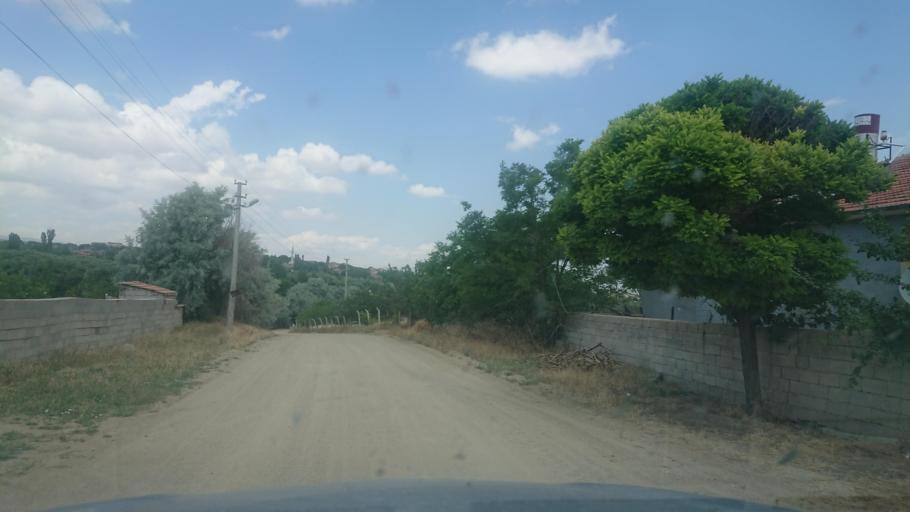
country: TR
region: Aksaray
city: Agacoren
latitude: 38.9323
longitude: 33.9563
